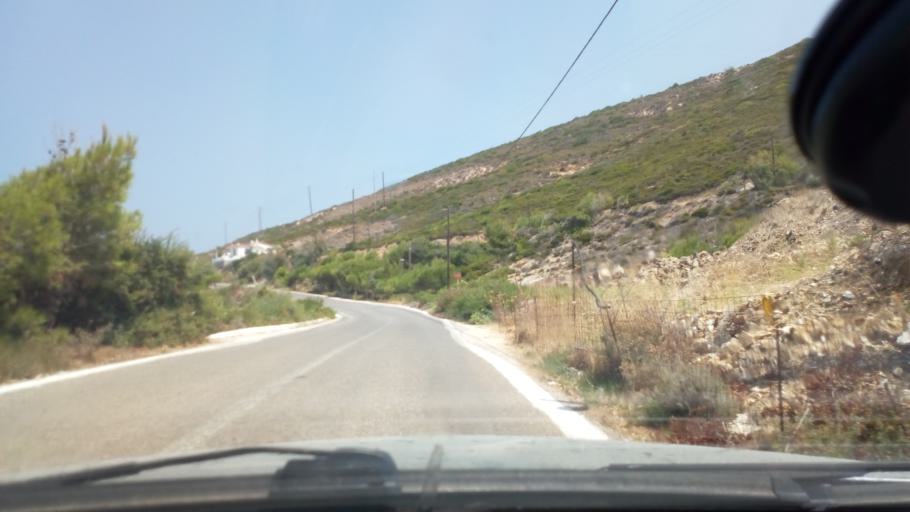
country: GR
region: North Aegean
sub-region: Nomos Samou
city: Agios Kirykos
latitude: 37.6310
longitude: 26.1100
